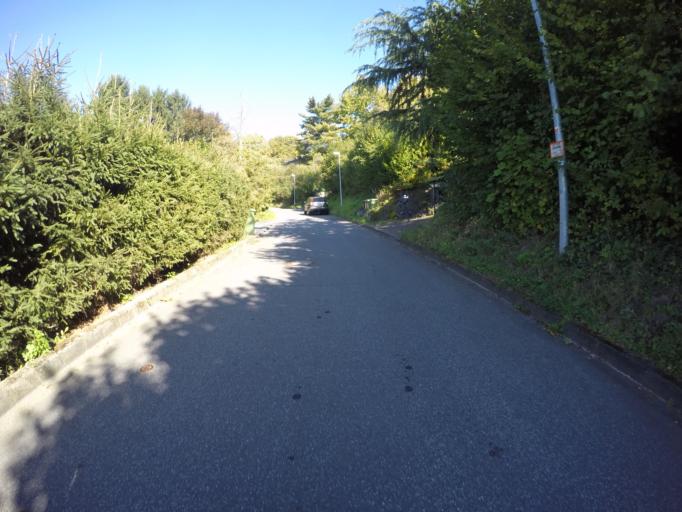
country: DE
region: Rheinland-Pfalz
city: Melsbach
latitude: 50.4776
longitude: 7.4775
